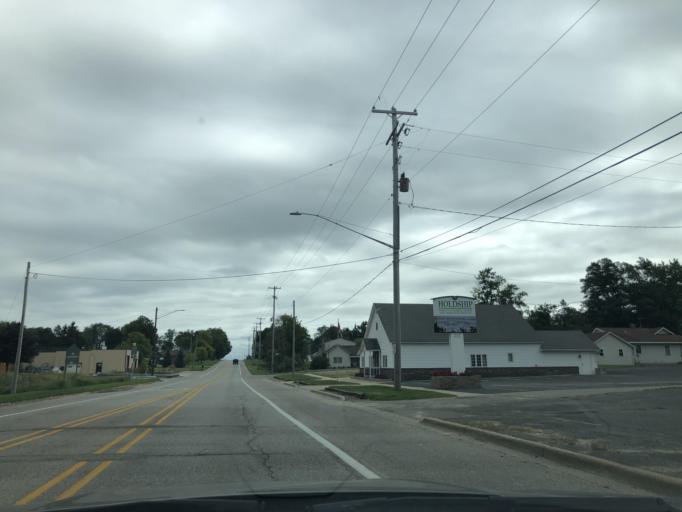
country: US
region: Michigan
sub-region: Missaukee County
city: Lake City
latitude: 44.1937
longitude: -85.2086
